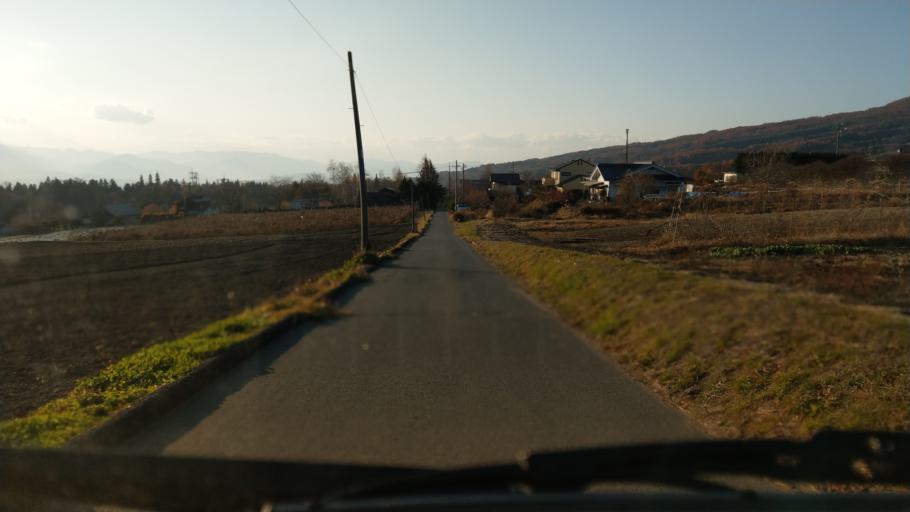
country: JP
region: Nagano
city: Komoro
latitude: 36.3518
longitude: 138.4524
